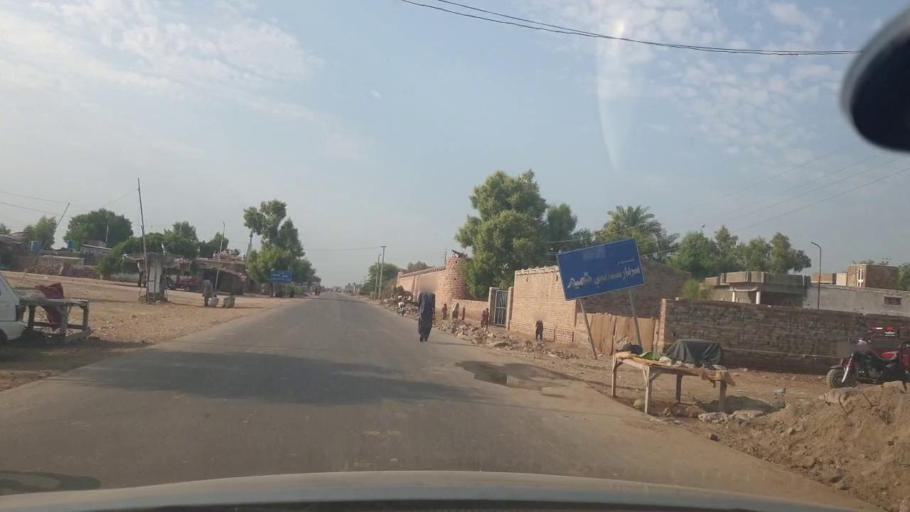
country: PK
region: Sindh
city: Jacobabad
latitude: 28.1090
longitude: 68.3264
